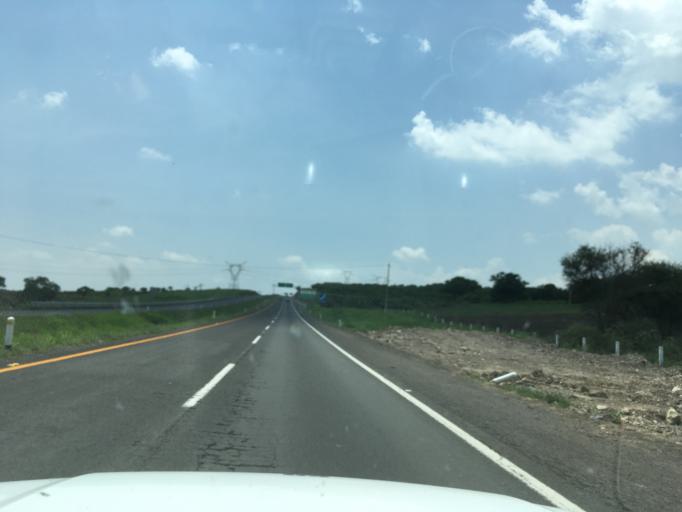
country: MX
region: Jalisco
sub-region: Zapotlanejo
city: La Mezquitera
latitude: 20.5777
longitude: -103.0901
